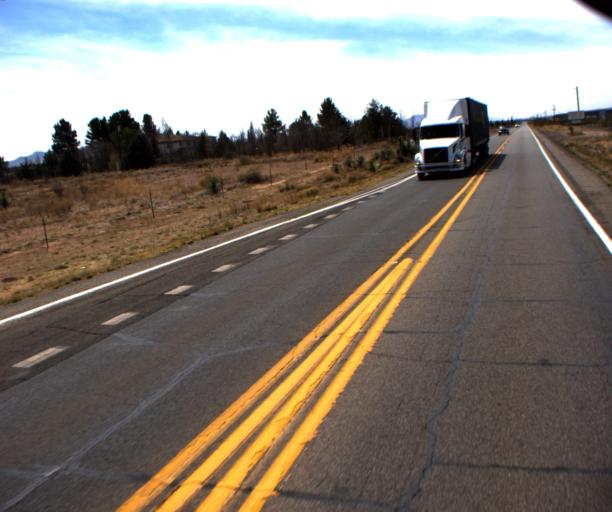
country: US
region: Arizona
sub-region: Cochise County
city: Pirtleville
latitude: 31.3708
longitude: -109.5794
